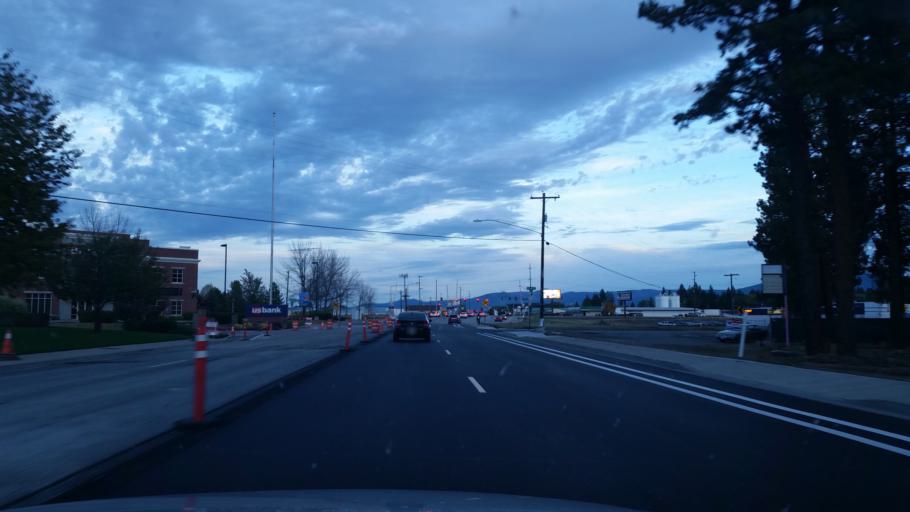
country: US
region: Washington
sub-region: Spokane County
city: Dishman
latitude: 47.6554
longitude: -117.2851
